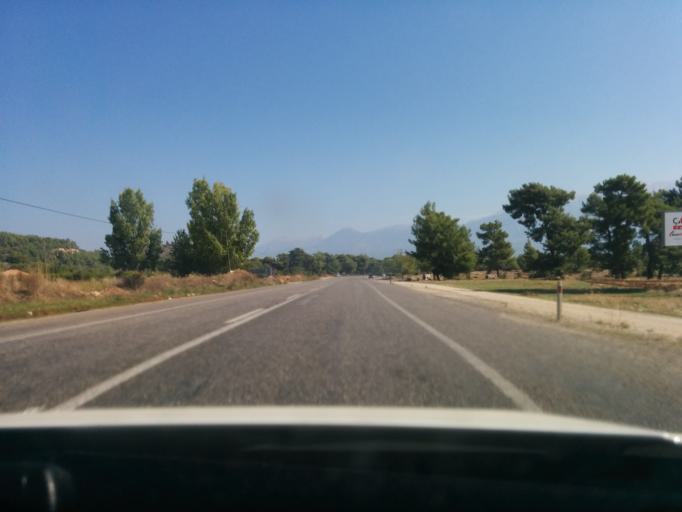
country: TR
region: Mugla
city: Esen
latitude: 36.4760
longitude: 29.3026
